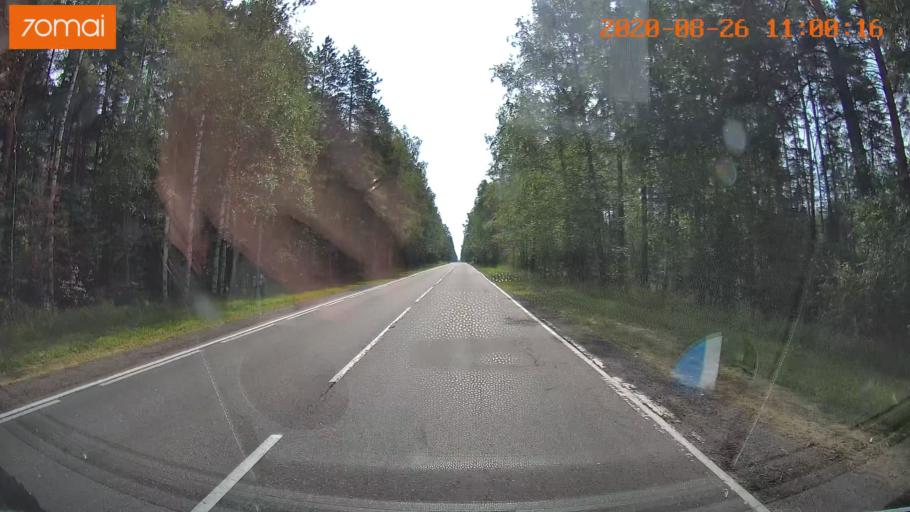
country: RU
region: Rjazan
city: Izhevskoye
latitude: 54.5762
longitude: 41.2119
